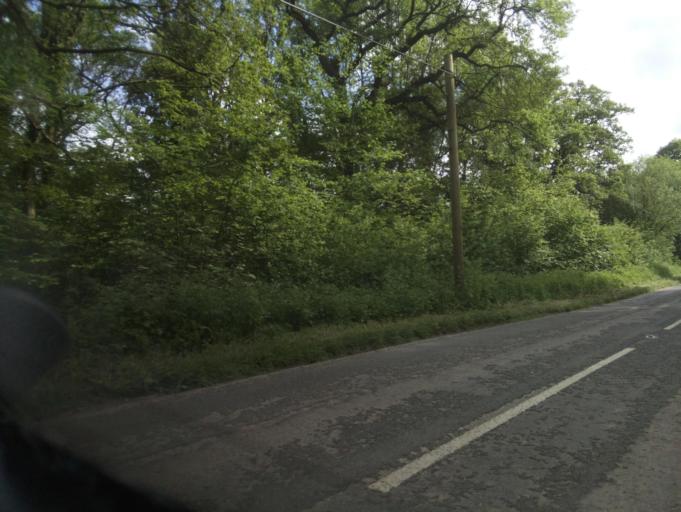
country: GB
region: England
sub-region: Herefordshire
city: Evesbatch
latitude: 52.1125
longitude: -2.4075
